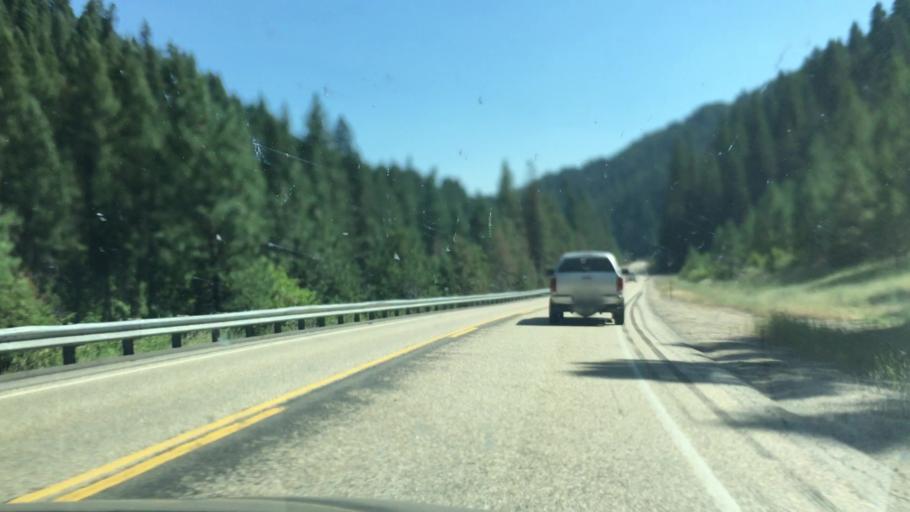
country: US
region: Idaho
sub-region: Valley County
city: Cascade
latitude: 44.1638
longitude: -116.1181
